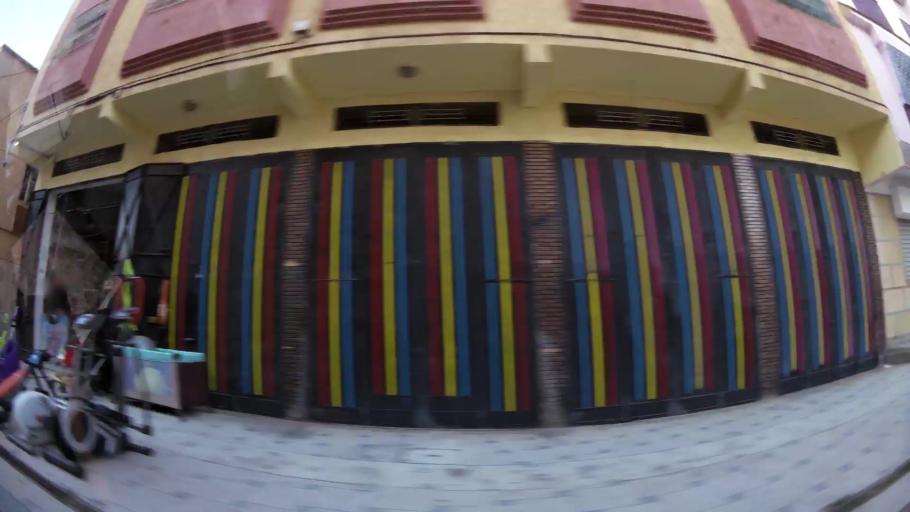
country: MA
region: Oriental
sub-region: Oujda-Angad
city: Oujda
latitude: 34.6762
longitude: -1.9008
